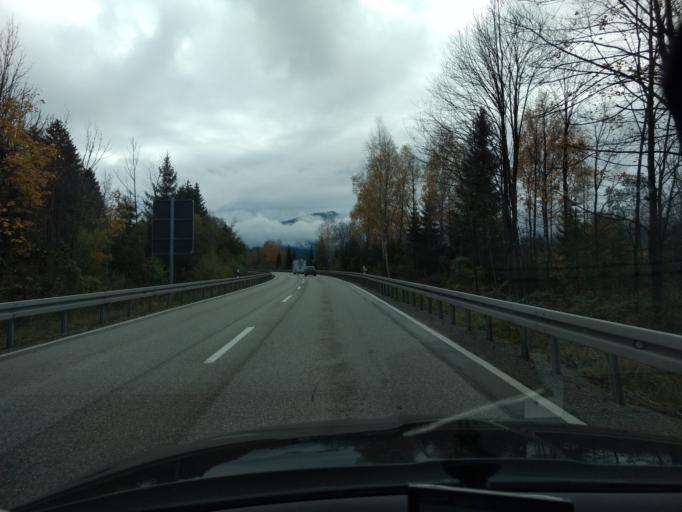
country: DE
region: Bavaria
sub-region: Upper Bavaria
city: Lenggries
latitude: 47.6702
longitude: 11.5760
